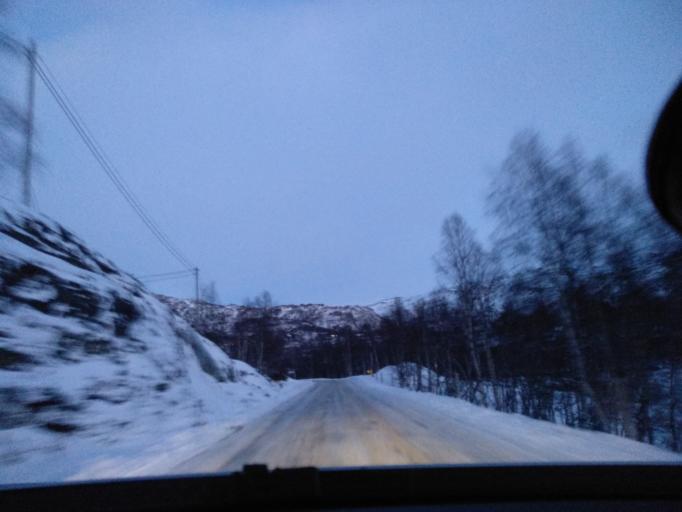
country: NO
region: Vest-Agder
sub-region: Sirdal
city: Tonstad
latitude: 59.0180
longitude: 6.9329
